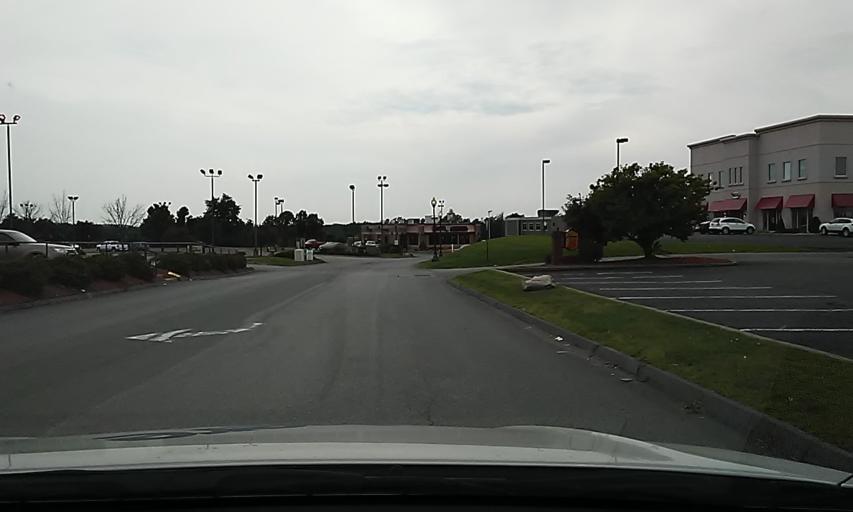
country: US
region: West Virginia
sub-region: Monongalia County
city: Brookhaven
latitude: 39.6487
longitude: -79.8967
